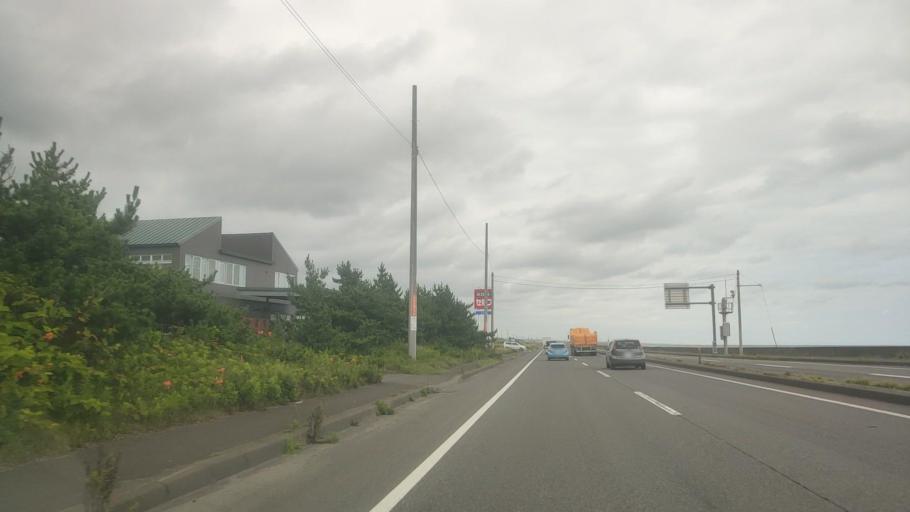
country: JP
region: Hokkaido
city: Shiraoi
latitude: 42.5514
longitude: 141.3675
